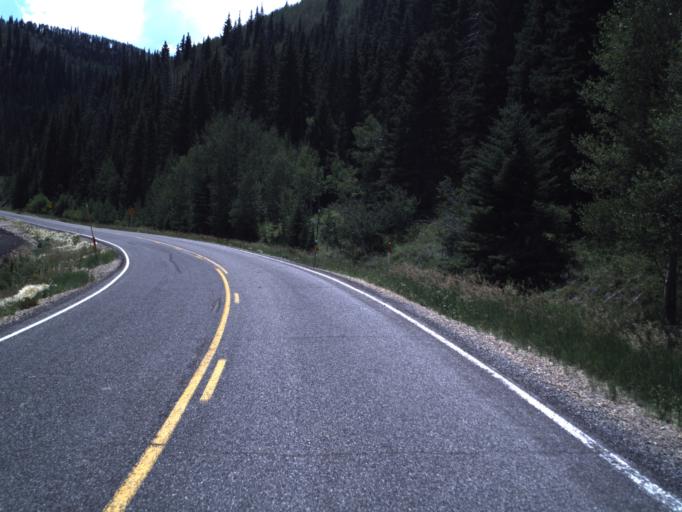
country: US
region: Utah
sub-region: Sanpete County
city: Fairview
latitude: 39.6708
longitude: -111.1555
